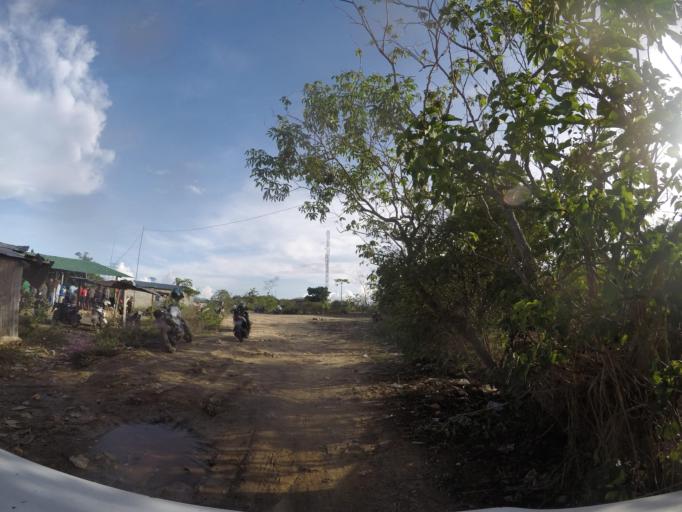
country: TL
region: Baucau
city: Baucau
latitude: -8.4860
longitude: 126.4534
